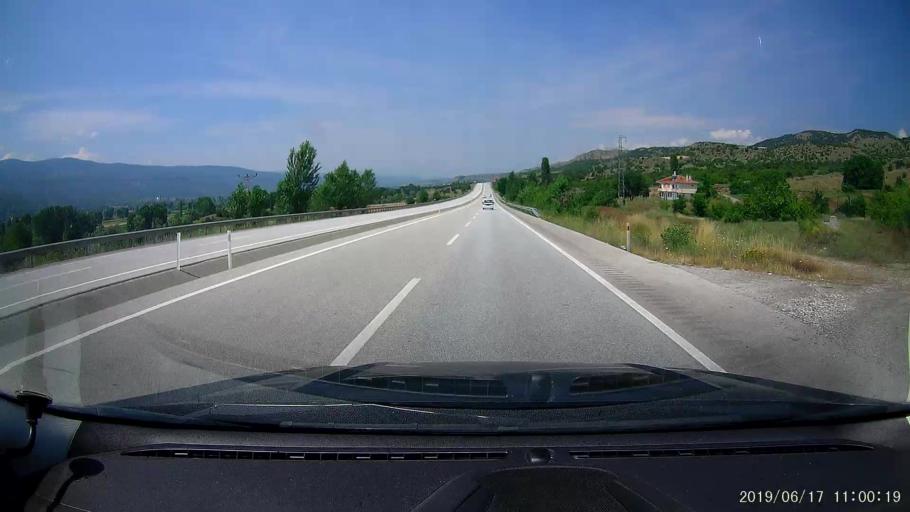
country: TR
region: Kastamonu
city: Tosya
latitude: 41.0354
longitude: 34.1835
